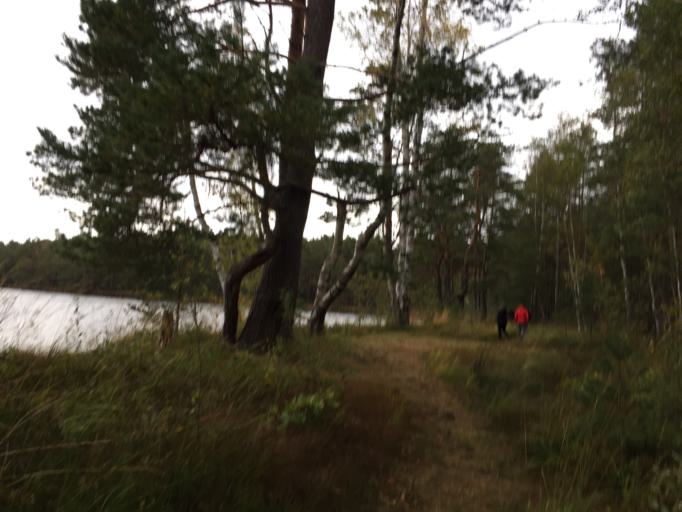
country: LV
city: Tireli
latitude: 56.9688
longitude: 23.5307
